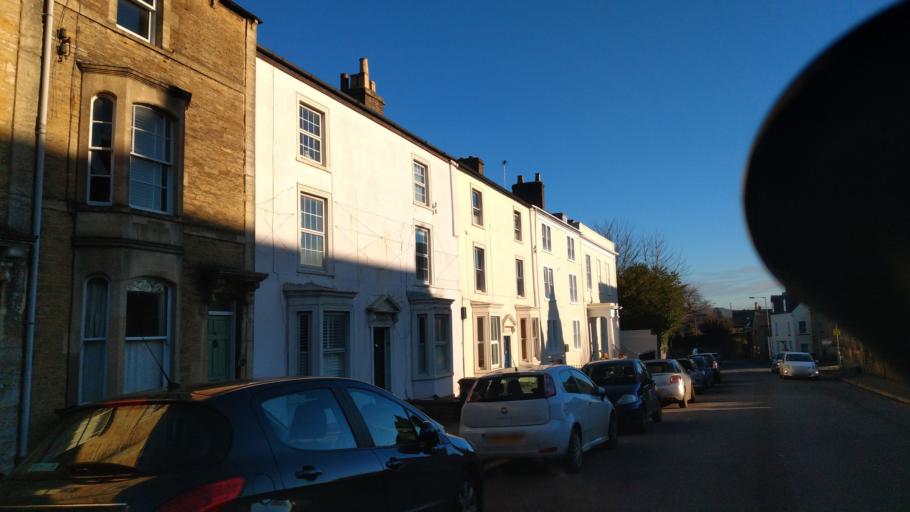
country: GB
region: England
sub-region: Somerset
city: Frome
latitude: 51.2282
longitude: -2.3160
